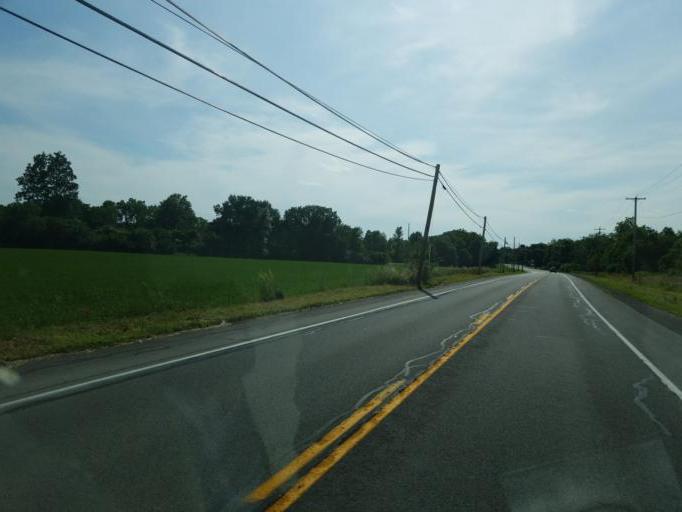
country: US
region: New York
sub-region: Livingston County
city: Caledonia
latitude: 42.9785
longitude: -77.8895
